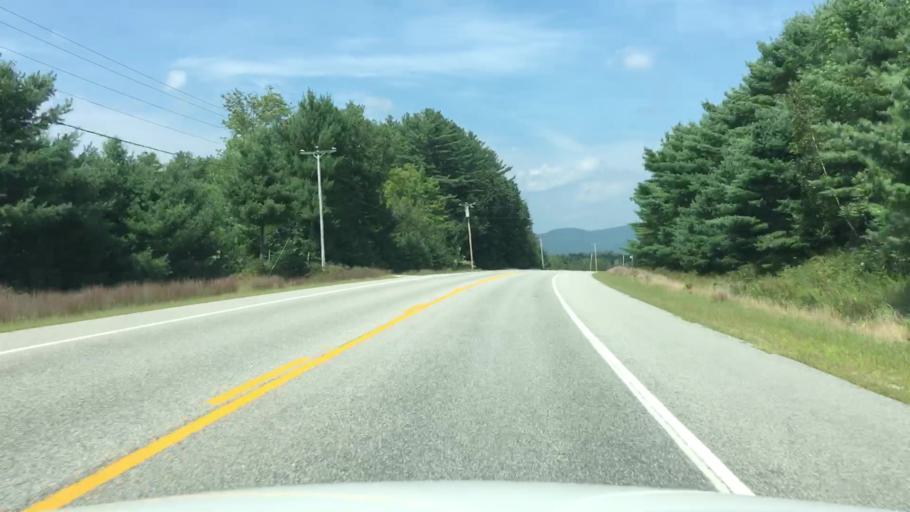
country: US
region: Maine
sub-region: Oxford County
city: Canton
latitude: 44.4581
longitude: -70.3199
